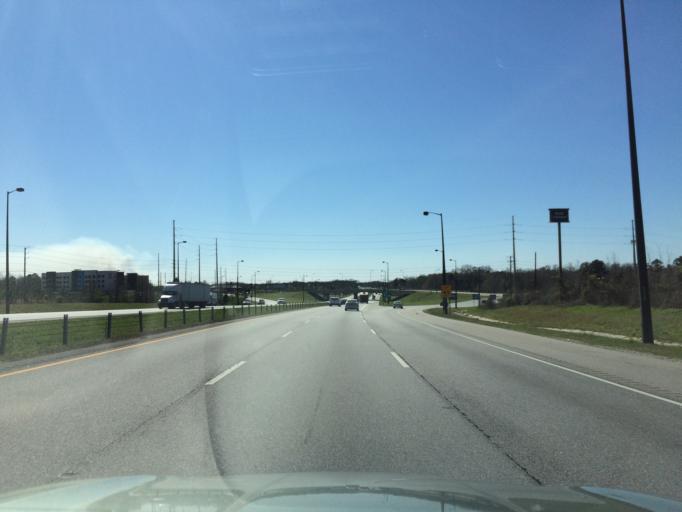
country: US
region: Alabama
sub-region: Lee County
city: Auburn
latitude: 32.5612
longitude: -85.5012
